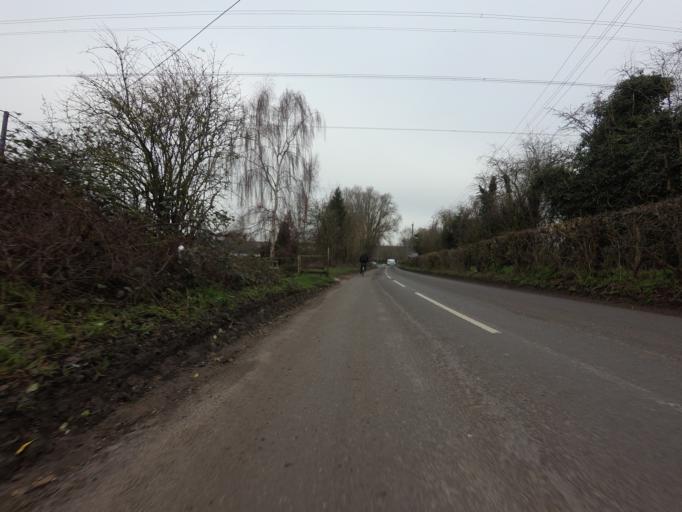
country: GB
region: England
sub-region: Kent
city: Eynsford
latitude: 51.3985
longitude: 0.2456
